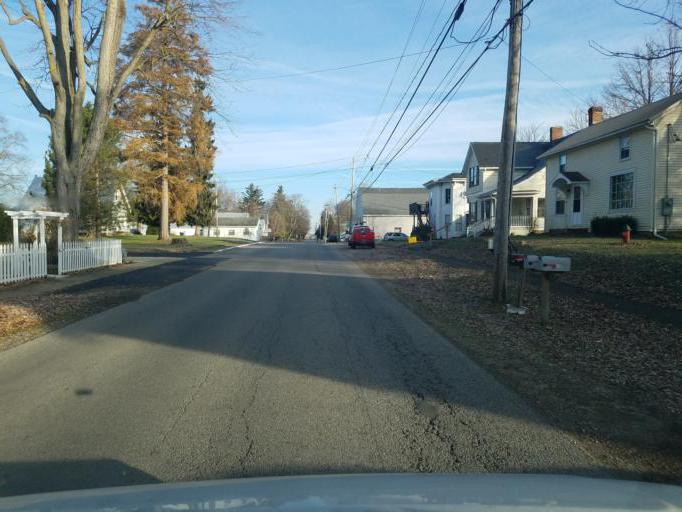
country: US
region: Ohio
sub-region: Morrow County
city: Mount Gilead
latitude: 40.5569
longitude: -82.8626
